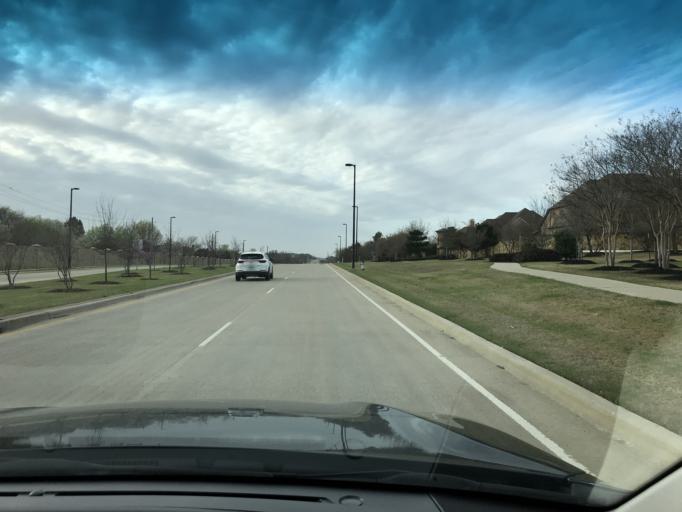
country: US
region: Texas
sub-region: Tarrant County
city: Southlake
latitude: 32.9446
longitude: -97.1861
